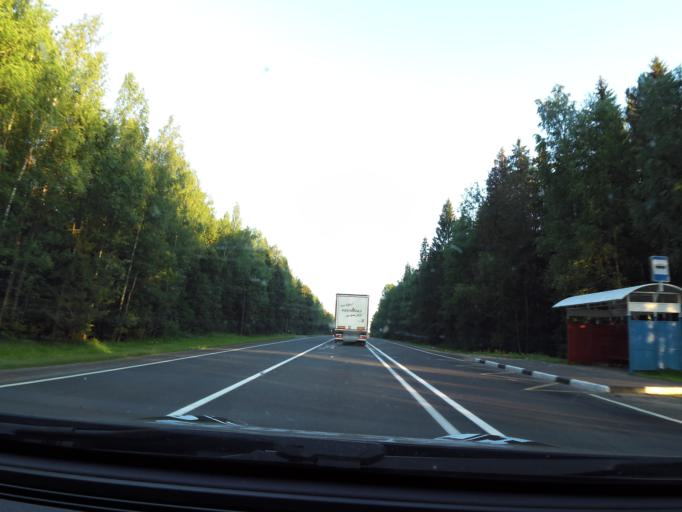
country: RU
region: Jaroslavl
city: Prechistoye
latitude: 58.4459
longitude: 40.3210
